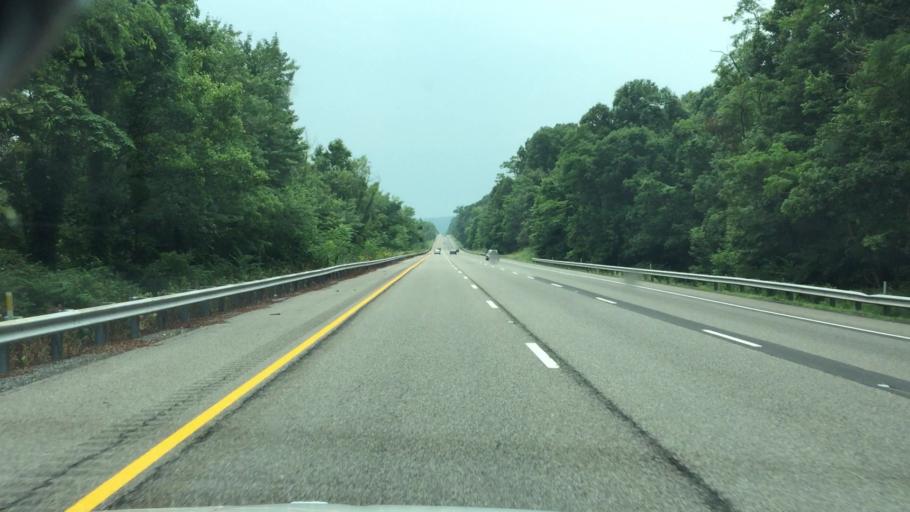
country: US
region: West Virginia
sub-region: Morgan County
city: Berkeley Springs
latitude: 39.6864
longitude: -78.4034
